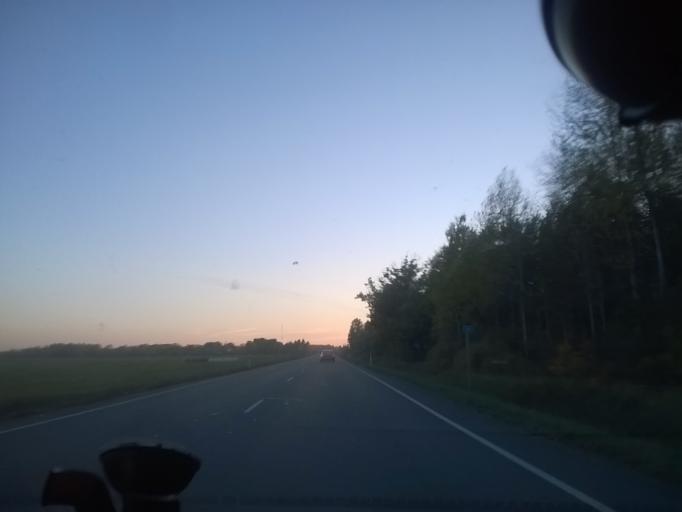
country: EE
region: Laeaene
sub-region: Ridala Parish
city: Uuemoisa
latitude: 58.9664
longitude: 23.8319
